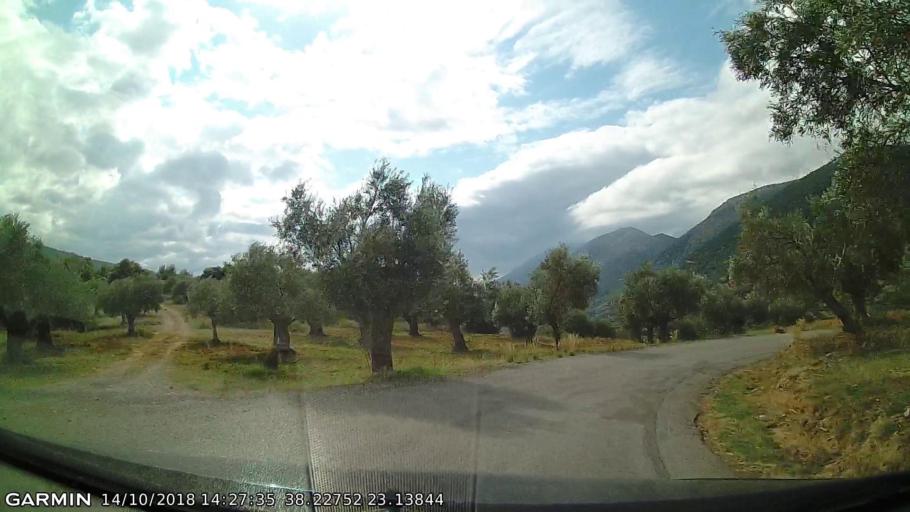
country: GR
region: Central Greece
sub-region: Nomos Voiotias
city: Thespies
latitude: 38.2275
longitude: 23.1383
